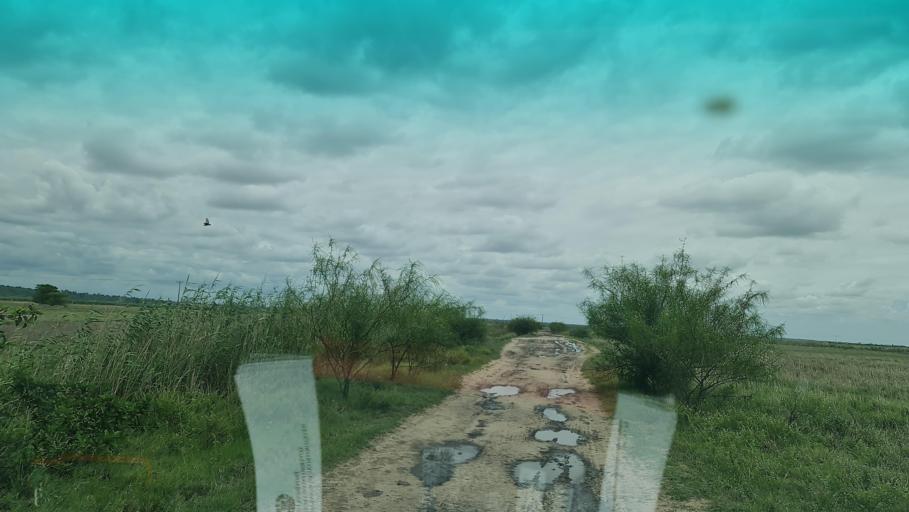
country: MZ
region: Maputo City
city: Maputo
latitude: -25.7265
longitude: 32.7017
